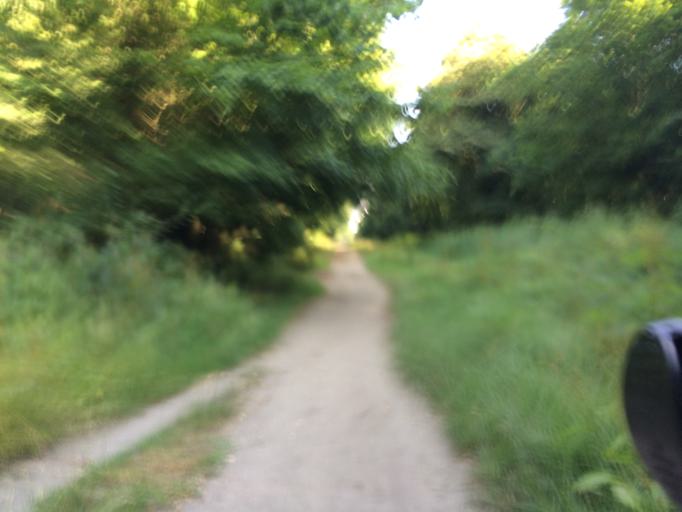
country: FR
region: Ile-de-France
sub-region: Departement de l'Essonne
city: Montgeron
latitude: 48.6845
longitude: 2.4427
